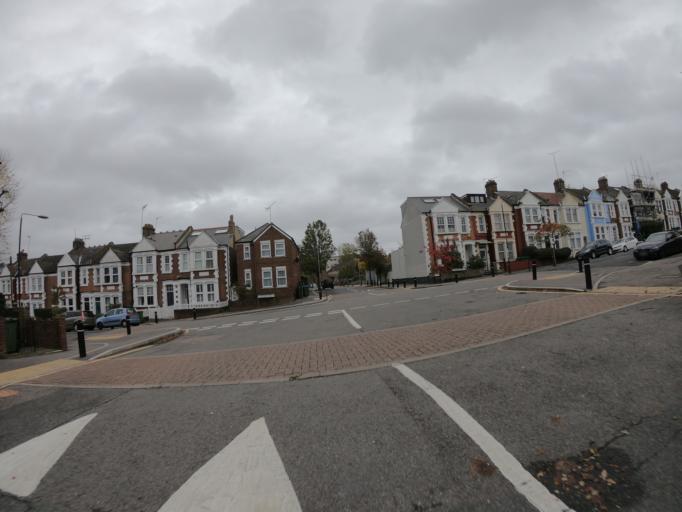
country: GB
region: England
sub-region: Greater London
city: Blackheath
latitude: 51.4815
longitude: 0.0262
